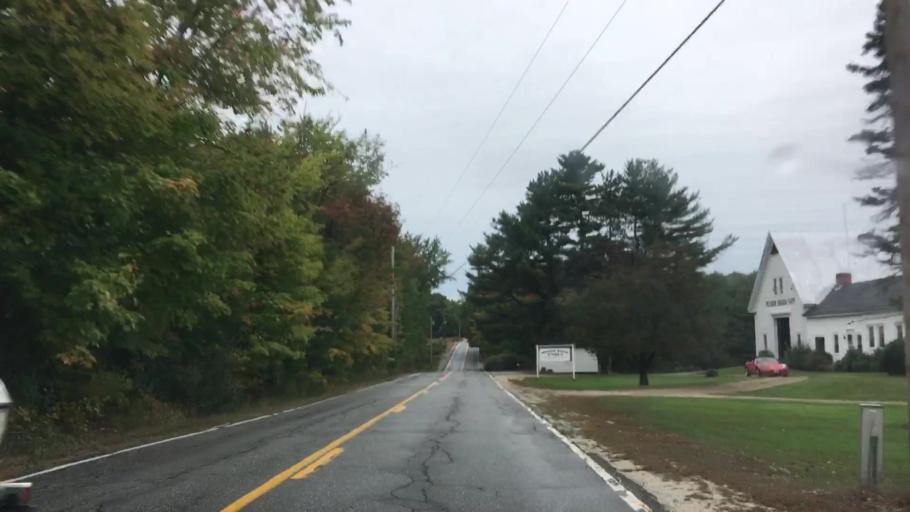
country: US
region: Maine
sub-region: Cumberland County
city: Raymond
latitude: 43.9714
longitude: -70.4684
